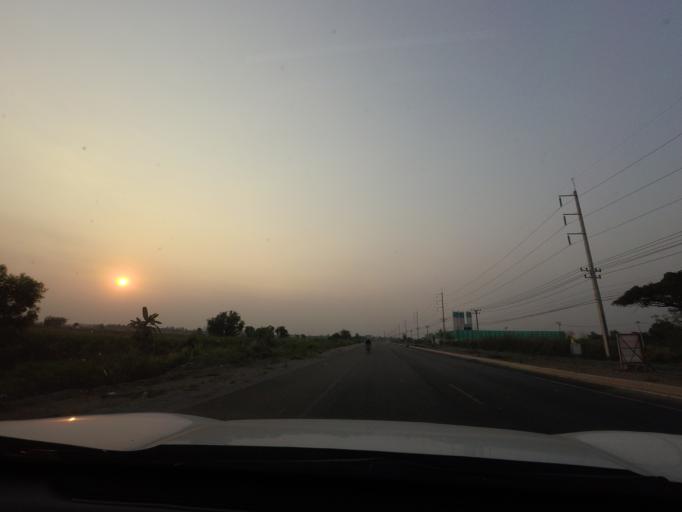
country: TH
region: Nakhon Nayok
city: Ongkharak
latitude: 14.1140
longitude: 101.0139
